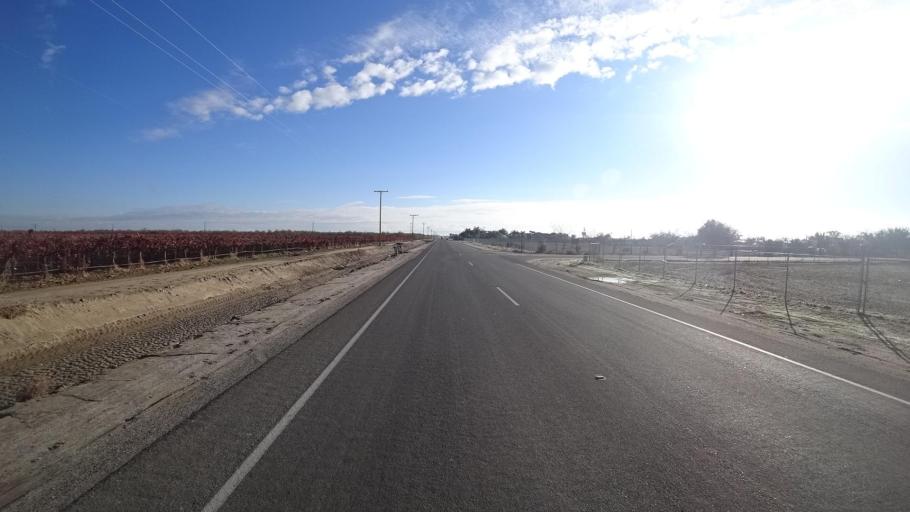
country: US
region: California
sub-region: Kern County
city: Delano
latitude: 35.7759
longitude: -119.2834
